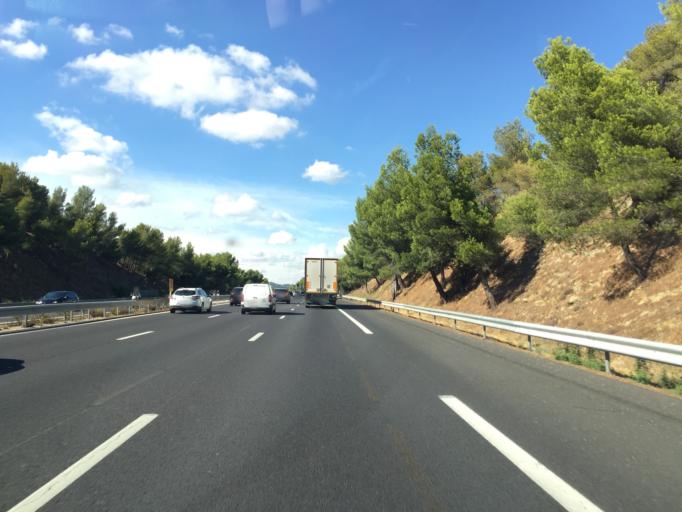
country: FR
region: Provence-Alpes-Cote d'Azur
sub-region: Departement des Bouches-du-Rhone
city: Salon-de-Provence
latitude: 43.6456
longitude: 5.1125
